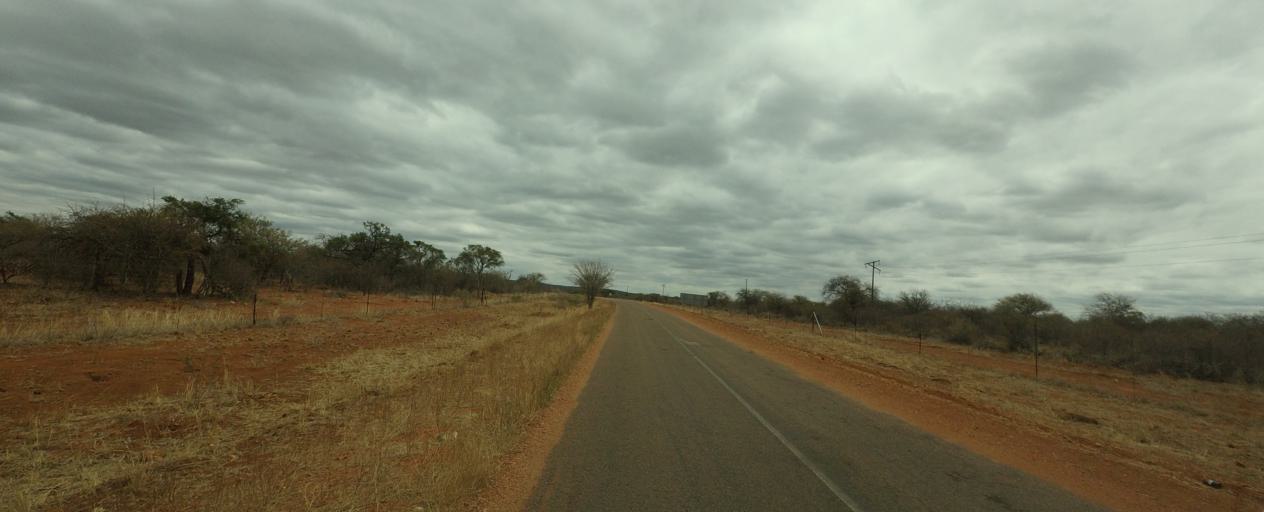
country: BW
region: Central
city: Mathathane
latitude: -22.7389
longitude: 28.4610
